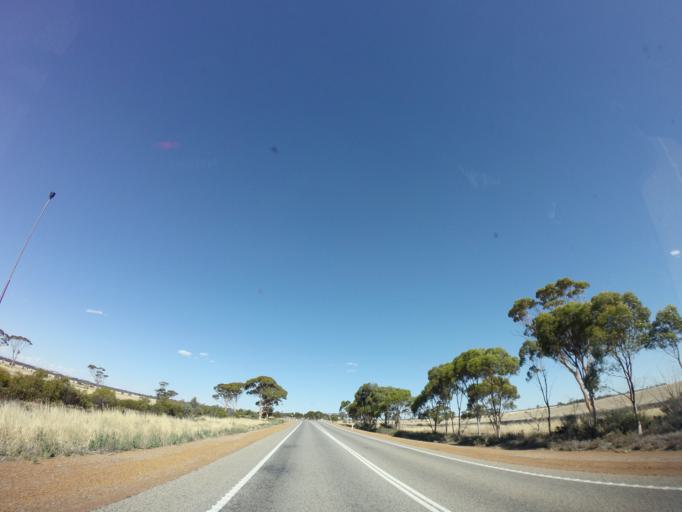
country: AU
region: Western Australia
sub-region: Merredin
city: Merredin
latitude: -31.5250
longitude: 118.1362
